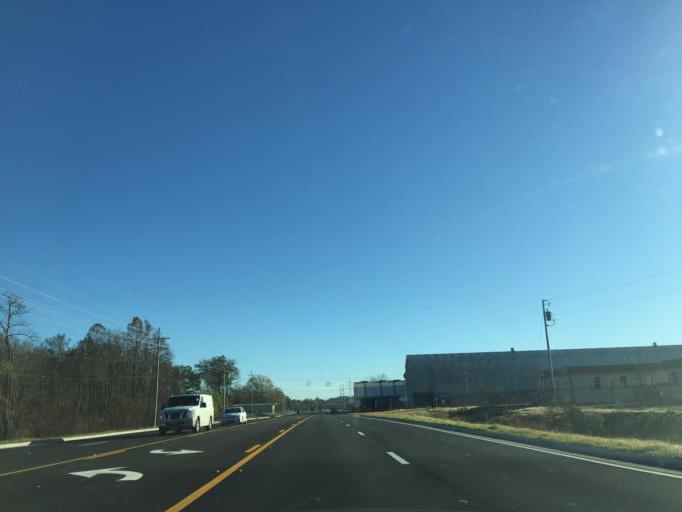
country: US
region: Mississippi
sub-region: Rankin County
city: Flowood
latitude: 32.3218
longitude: -90.1161
